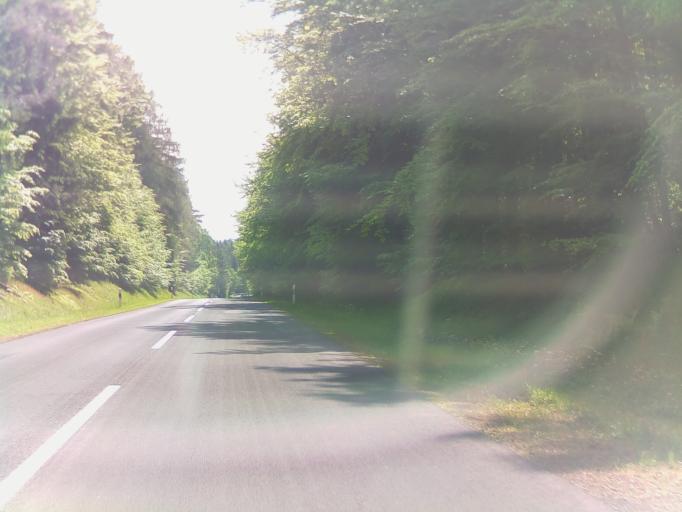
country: DE
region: Bavaria
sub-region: Regierungsbezirk Unterfranken
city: Bad Bocklet
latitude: 50.3436
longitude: 10.0836
